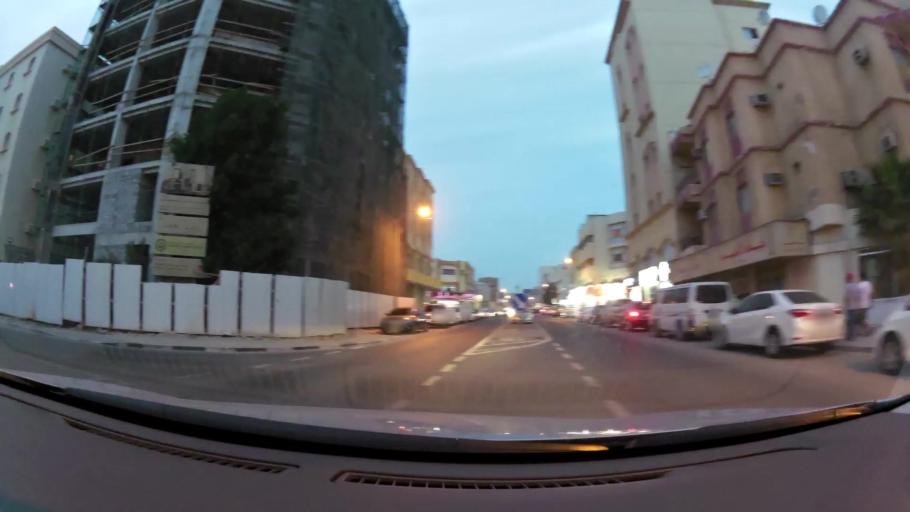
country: QA
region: Baladiyat ad Dawhah
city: Doha
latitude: 25.2695
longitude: 51.5237
